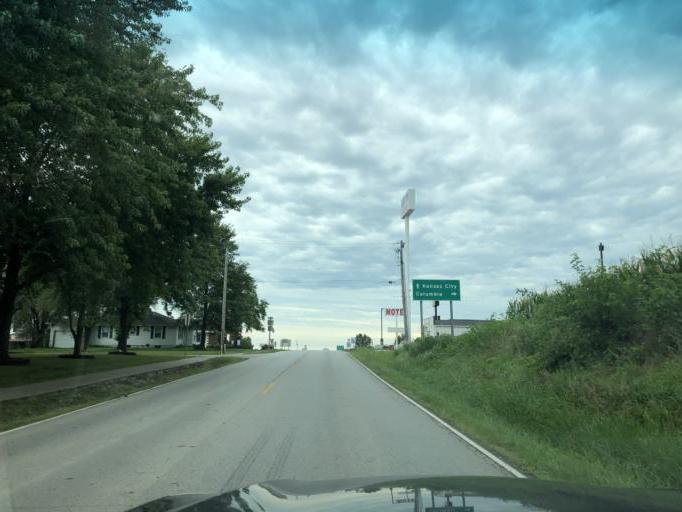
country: US
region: Missouri
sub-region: Saline County
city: Sweet Springs
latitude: 38.9749
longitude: -93.4151
